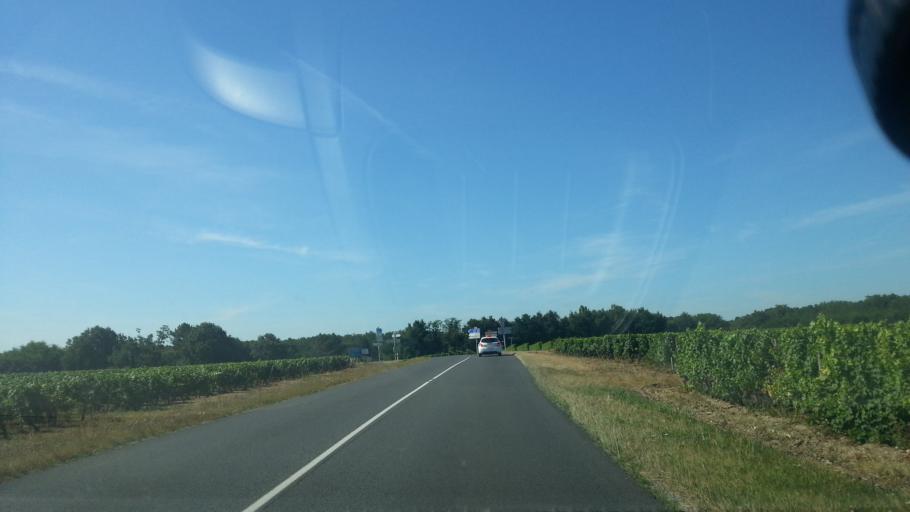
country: FR
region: Aquitaine
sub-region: Departement de la Gironde
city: Podensac
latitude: 44.6271
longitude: -0.3690
